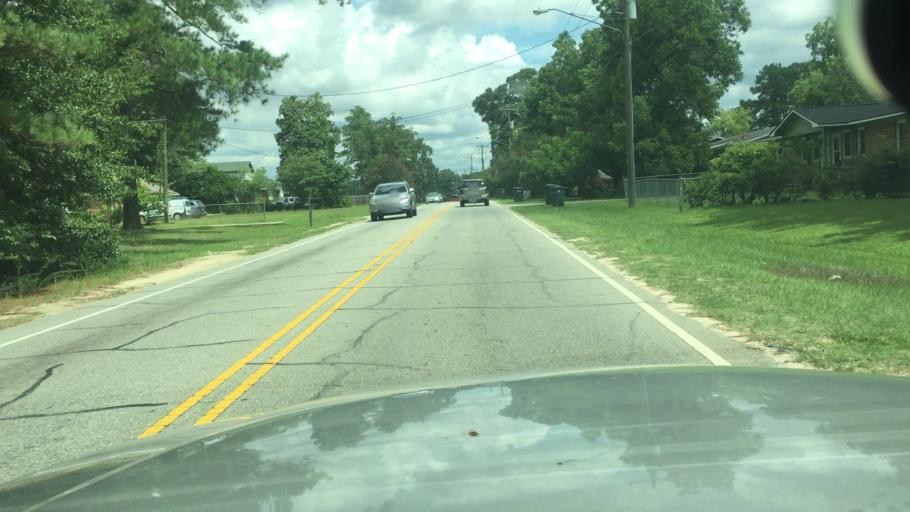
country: US
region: North Carolina
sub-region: Hoke County
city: Rockfish
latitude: 35.0364
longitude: -78.9973
